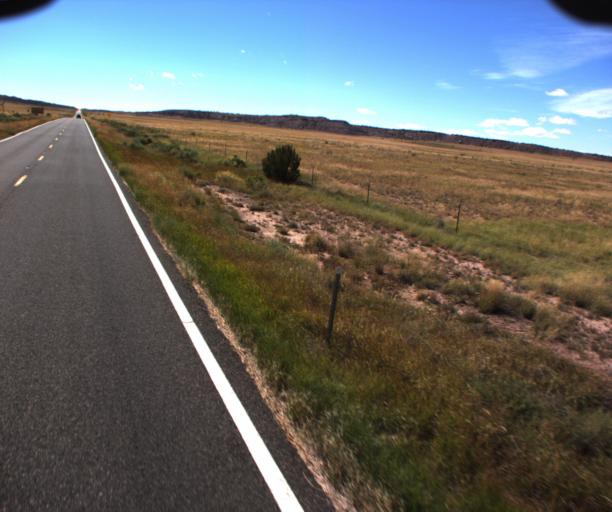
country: US
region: Arizona
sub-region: Apache County
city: Saint Johns
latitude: 34.6774
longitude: -109.2842
